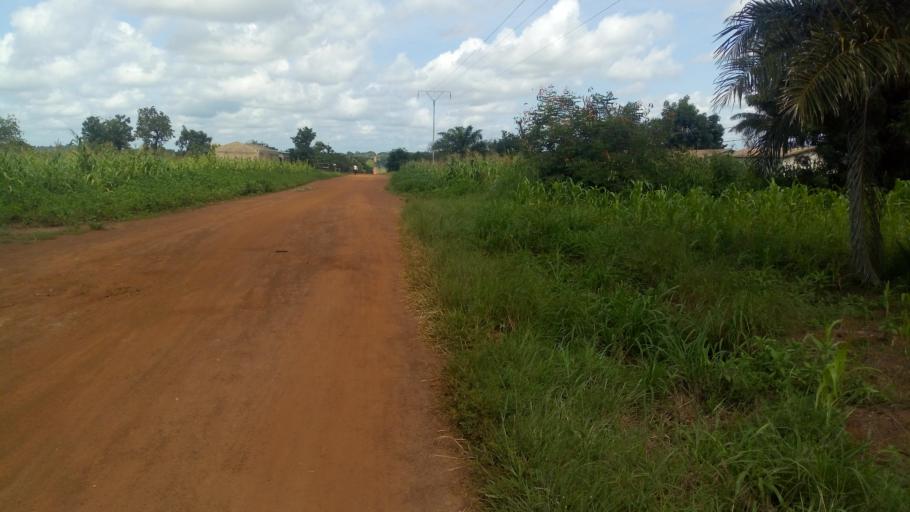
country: TG
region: Centrale
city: Sotouboua
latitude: 8.4329
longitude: 1.0023
